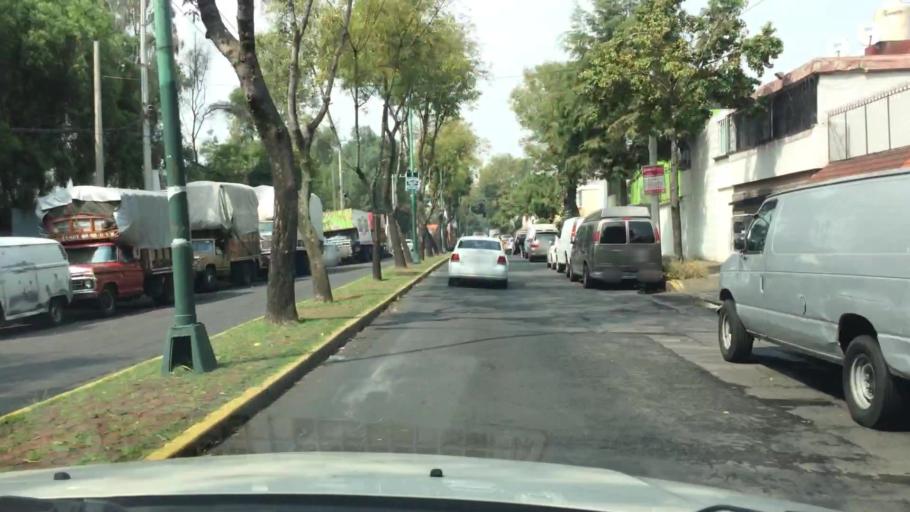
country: MX
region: Mexico City
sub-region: Iztacalco
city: Iztacalco
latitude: 19.4116
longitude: -99.1091
